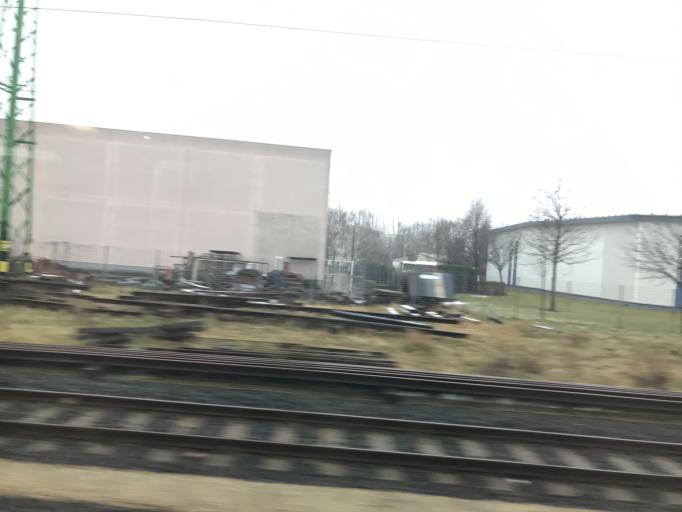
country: HU
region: Gyor-Moson-Sopron
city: Gyor
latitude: 47.6848
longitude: 17.6420
